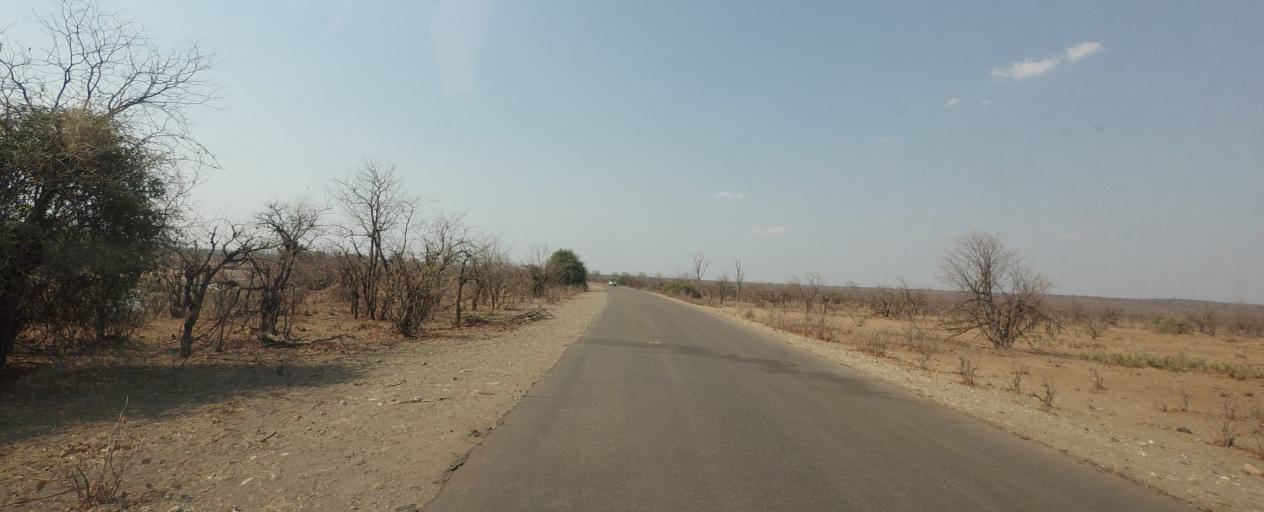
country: ZA
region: Limpopo
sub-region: Mopani District Municipality
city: Giyani
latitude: -23.1372
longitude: 31.3767
